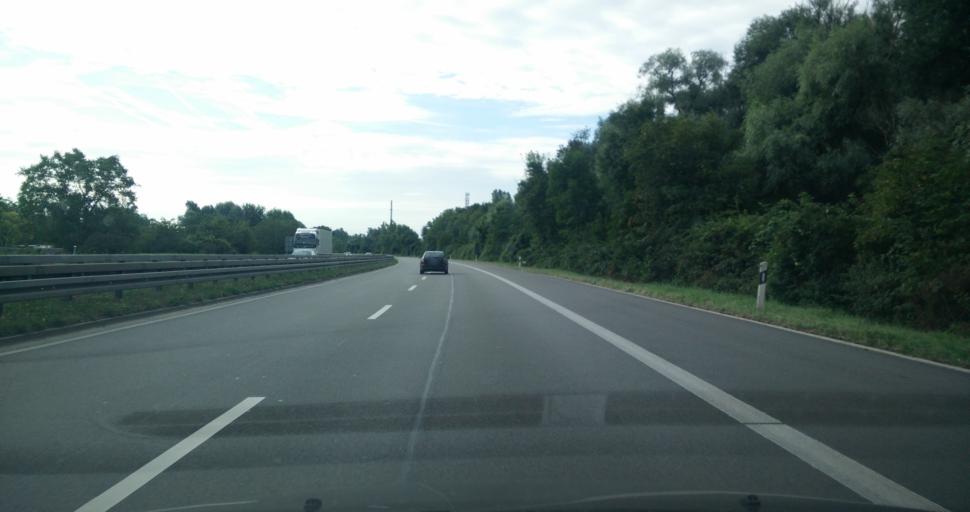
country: DE
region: Baden-Wuerttemberg
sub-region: Karlsruhe Region
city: Rheinstetten
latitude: 49.0287
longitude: 8.3324
